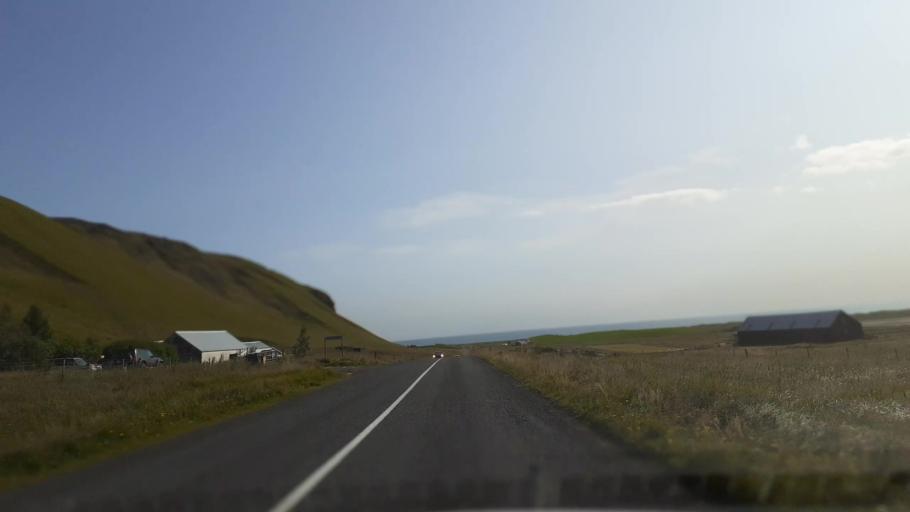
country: IS
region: South
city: Vestmannaeyjar
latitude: 63.4162
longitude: -19.0483
